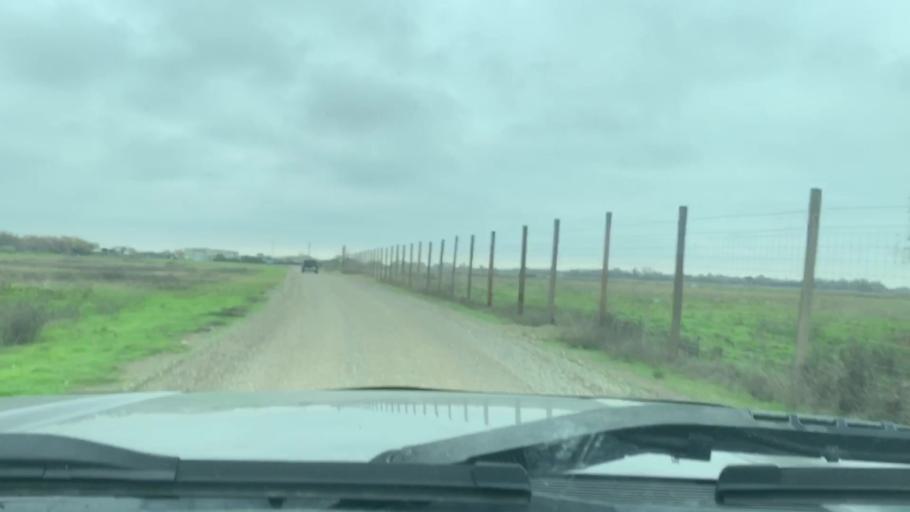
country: US
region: California
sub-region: Merced County
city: Los Banos
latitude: 37.1842
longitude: -120.7976
